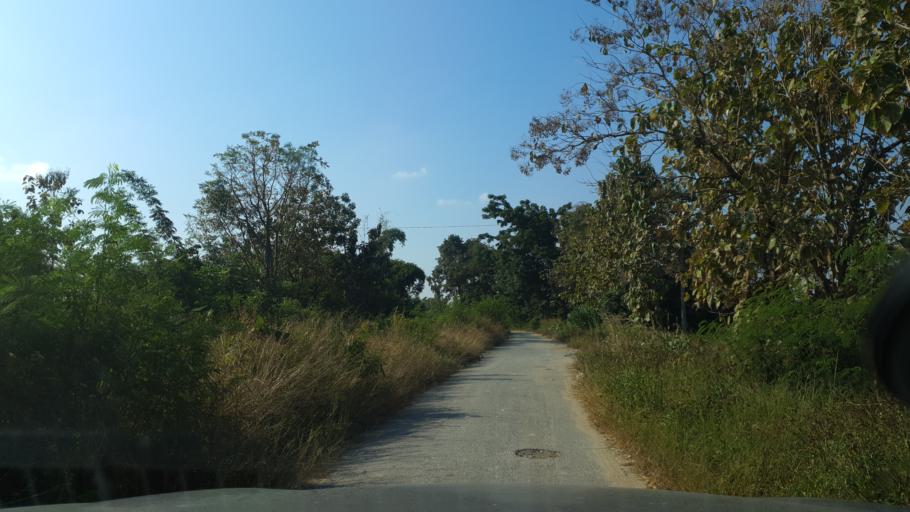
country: TH
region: Lamphun
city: Ban Thi
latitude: 18.6691
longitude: 99.1326
